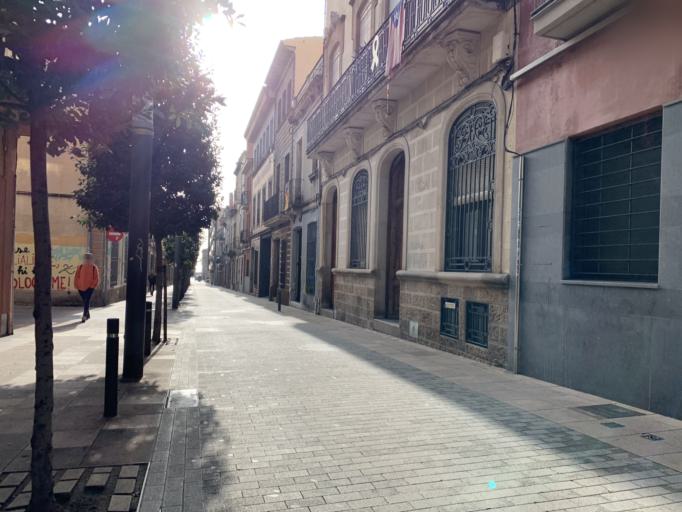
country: ES
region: Catalonia
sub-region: Provincia de Barcelona
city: Mataro
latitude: 41.5365
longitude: 2.4450
